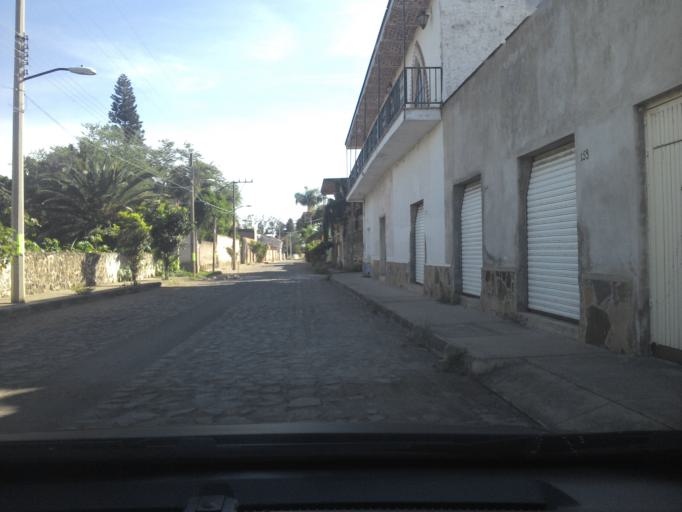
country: MX
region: Jalisco
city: Teuchitlan
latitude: 20.6860
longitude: -103.8452
